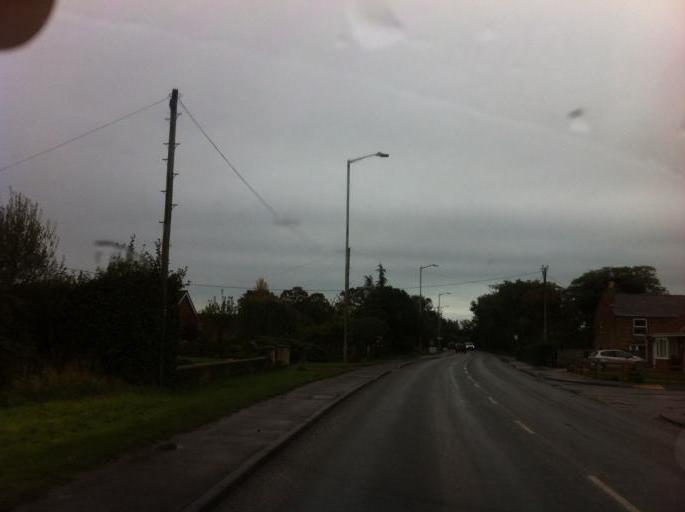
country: GB
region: England
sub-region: Lincolnshire
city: Wainfleet All Saints
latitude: 53.0388
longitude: 0.1240
